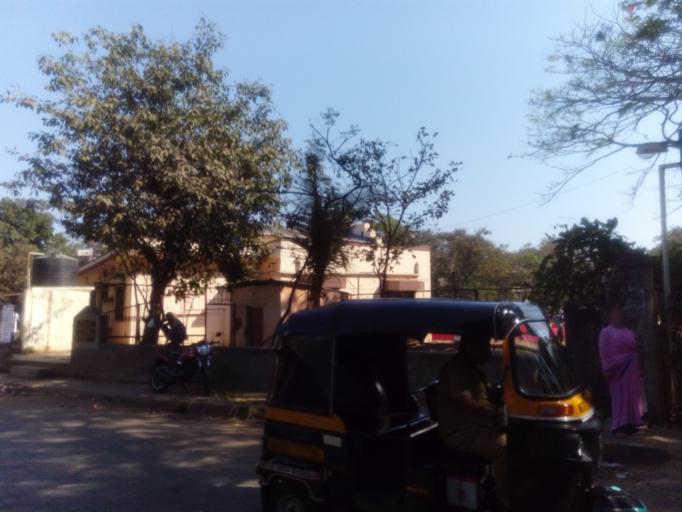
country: IN
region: Maharashtra
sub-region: Mumbai Suburban
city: Mumbai
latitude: 19.0890
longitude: 72.8409
